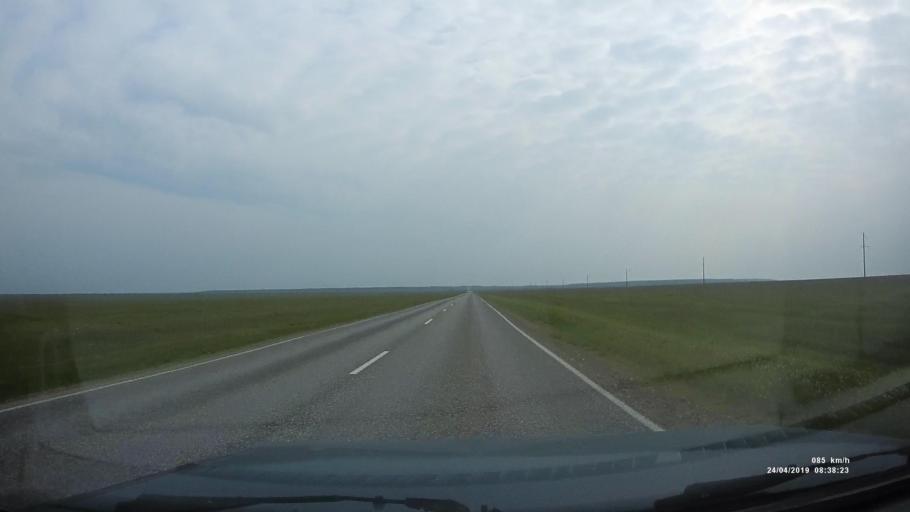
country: RU
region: Kalmykiya
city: Arshan'
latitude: 46.2150
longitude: 43.9662
